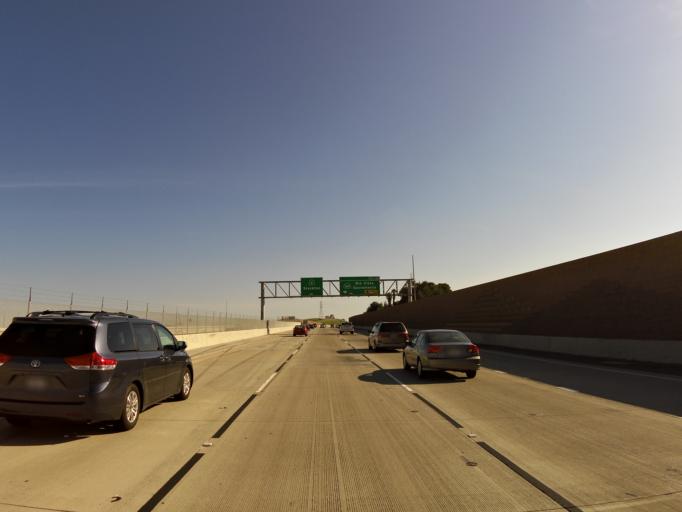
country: US
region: California
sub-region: Contra Costa County
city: Antioch
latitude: 37.9943
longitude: -121.7750
